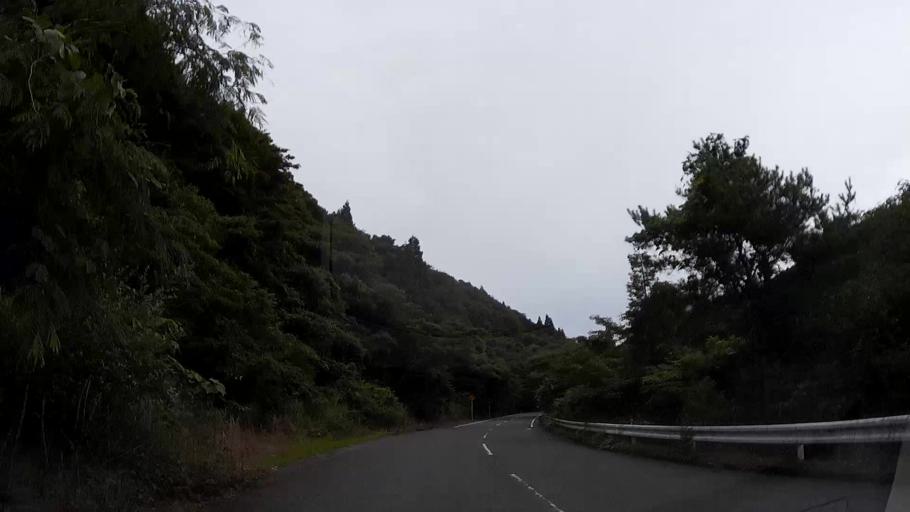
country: JP
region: Kumamoto
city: Kikuchi
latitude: 33.0582
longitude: 130.9025
